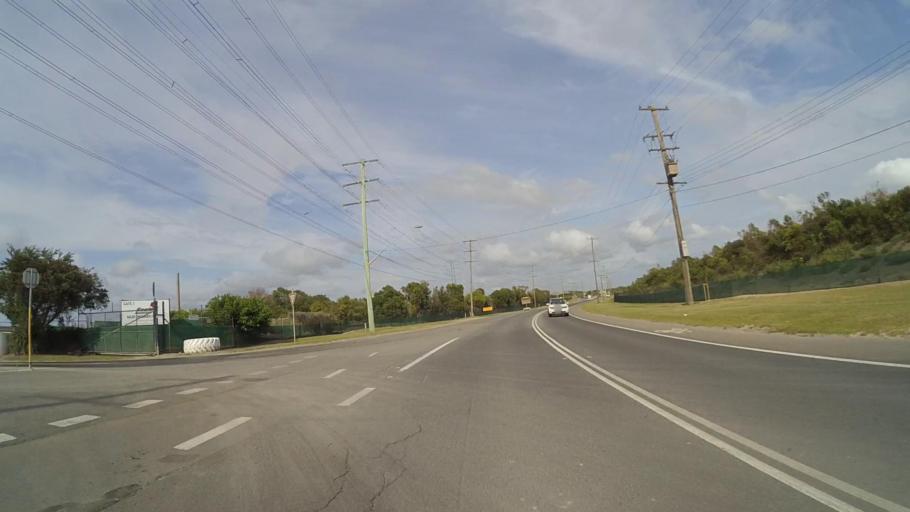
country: AU
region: New South Wales
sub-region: Sutherland Shire
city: Kurnell
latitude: -34.0245
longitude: 151.1892
